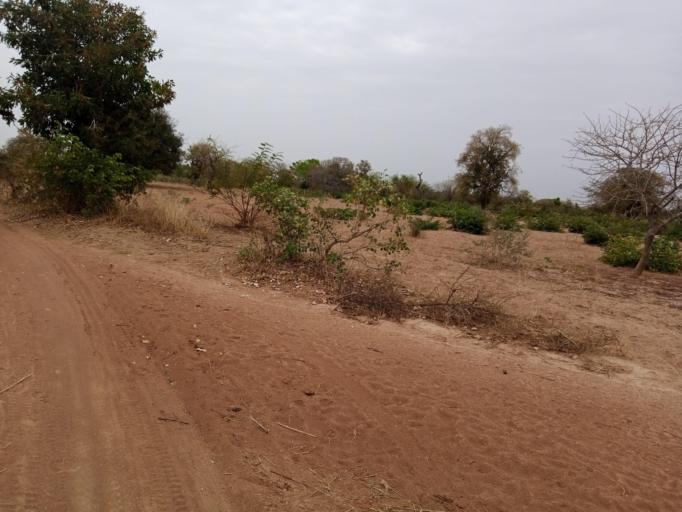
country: BF
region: Boucle du Mouhoun
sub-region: Province de la Kossi
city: Nouna
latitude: 12.8476
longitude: -4.0777
